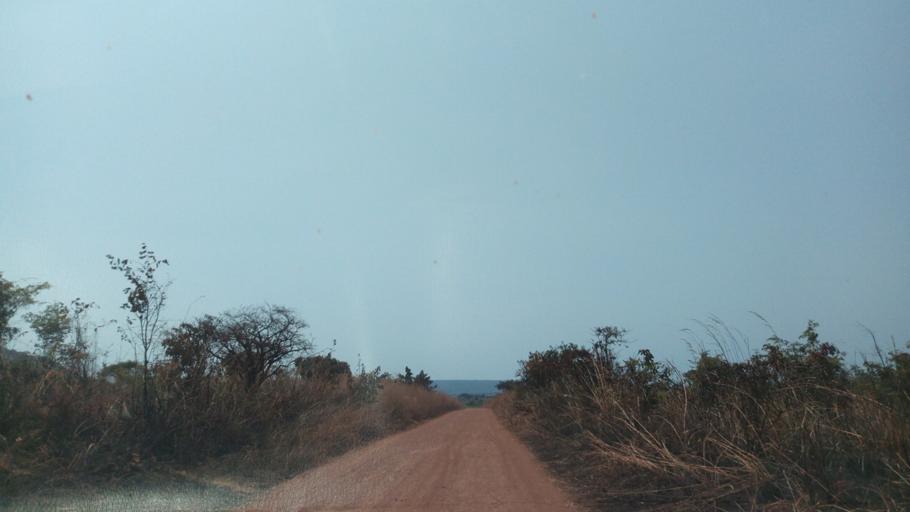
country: ZM
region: Luapula
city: Nchelenge
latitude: -8.7595
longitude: 28.6539
